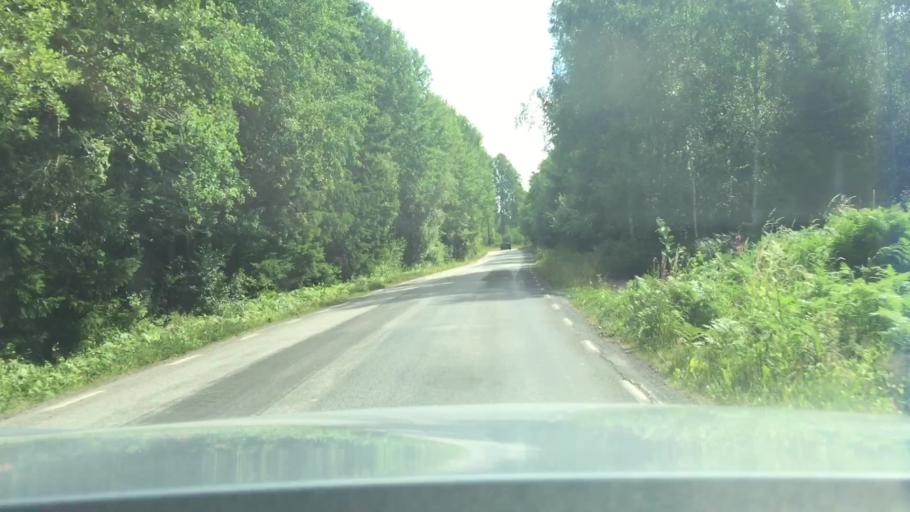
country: SE
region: Vaestra Goetaland
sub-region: Tidaholms Kommun
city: Olofstorp
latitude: 58.3431
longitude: 14.0293
